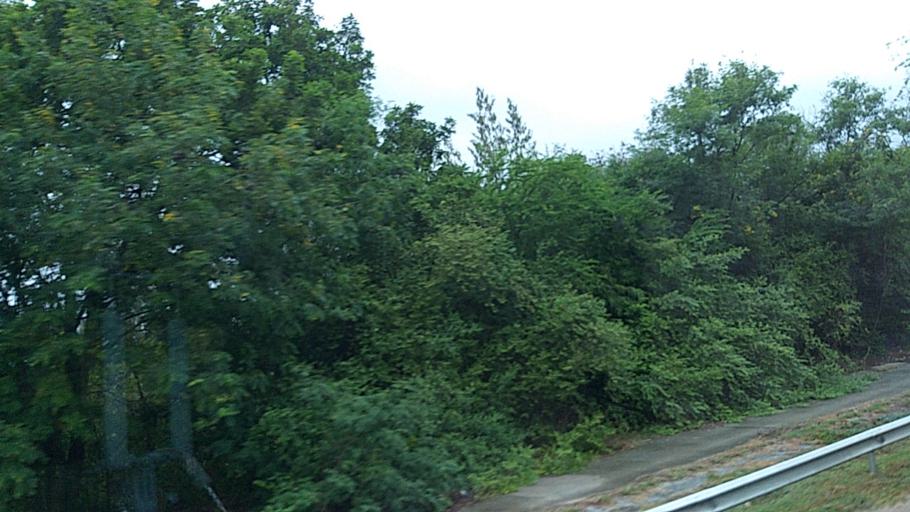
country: TH
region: Nakhon Ratchasima
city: Nakhon Ratchasima
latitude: 15.0542
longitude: 102.1585
